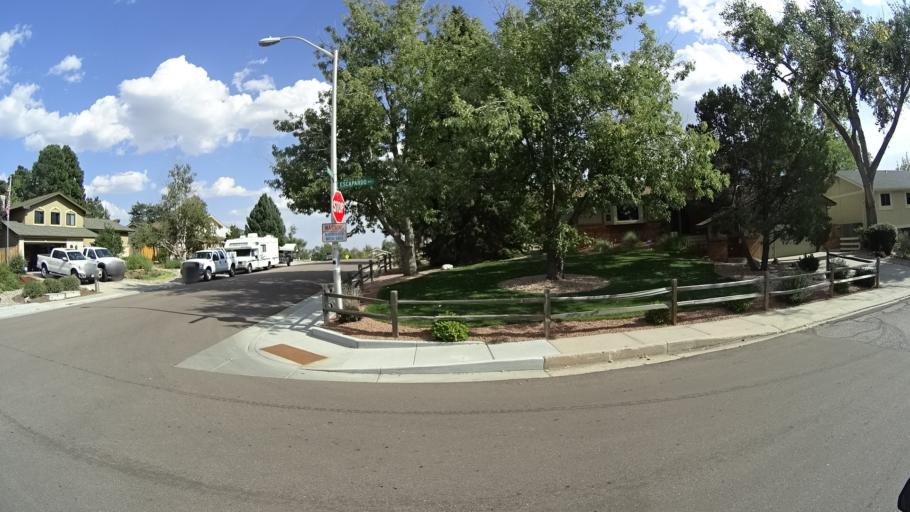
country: US
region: Colorado
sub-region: El Paso County
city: Cimarron Hills
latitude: 38.8733
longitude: -104.7322
